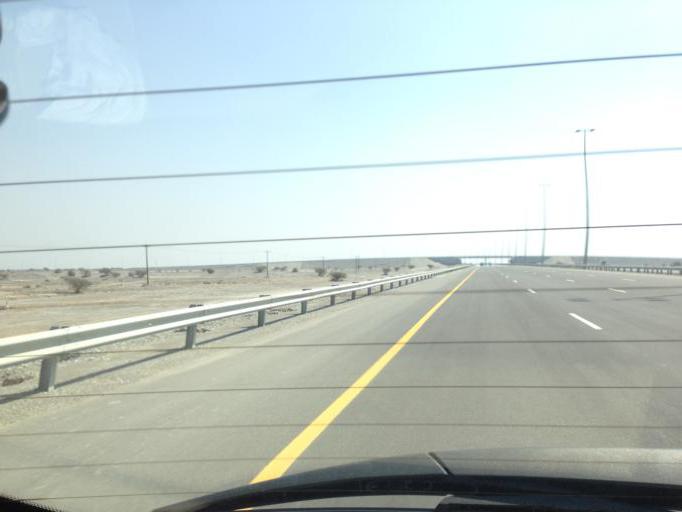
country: OM
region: Al Batinah
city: Barka'
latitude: 23.5757
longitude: 57.7647
